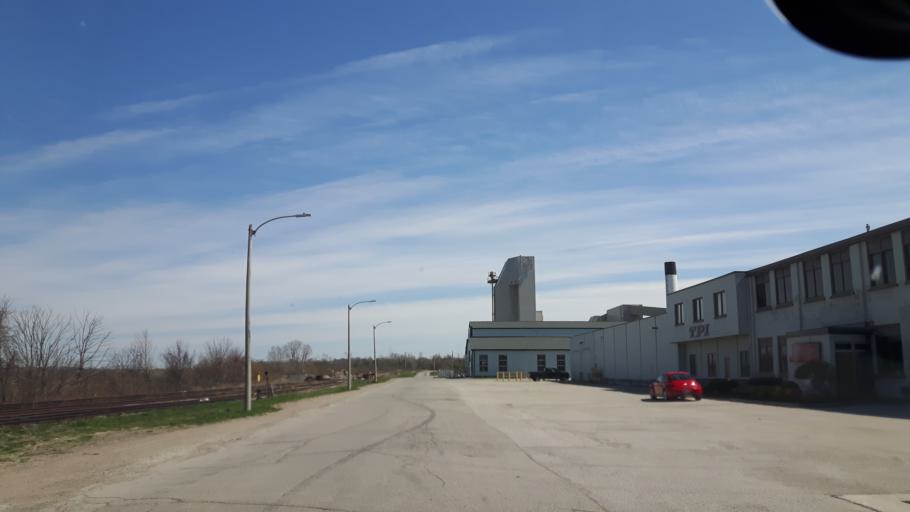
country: CA
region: Ontario
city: Goderich
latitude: 43.7412
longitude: -81.6985
